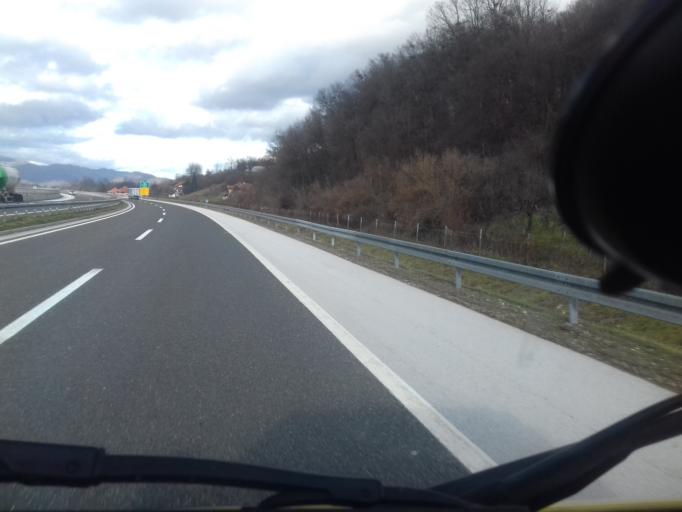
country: BA
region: Federation of Bosnia and Herzegovina
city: Visoko
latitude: 44.0017
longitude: 18.1796
